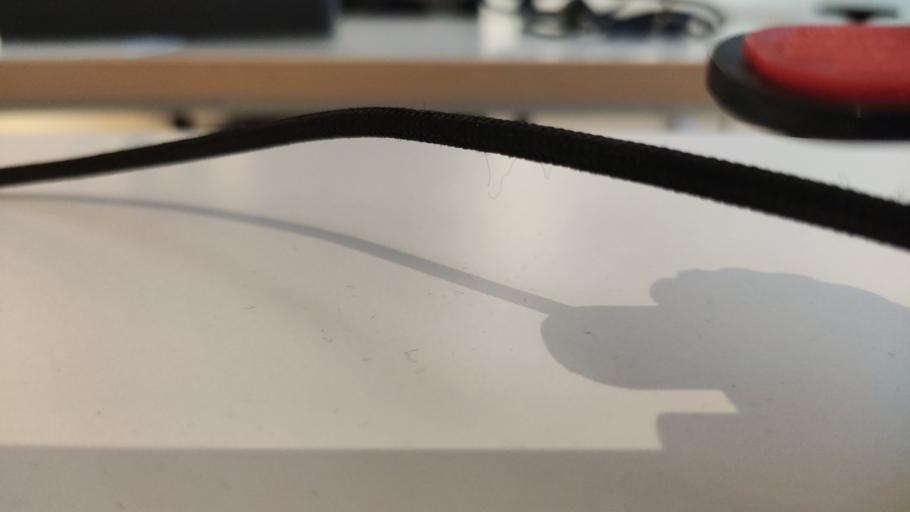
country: RU
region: Moskovskaya
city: Novopetrovskoye
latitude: 55.8589
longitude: 36.3812
